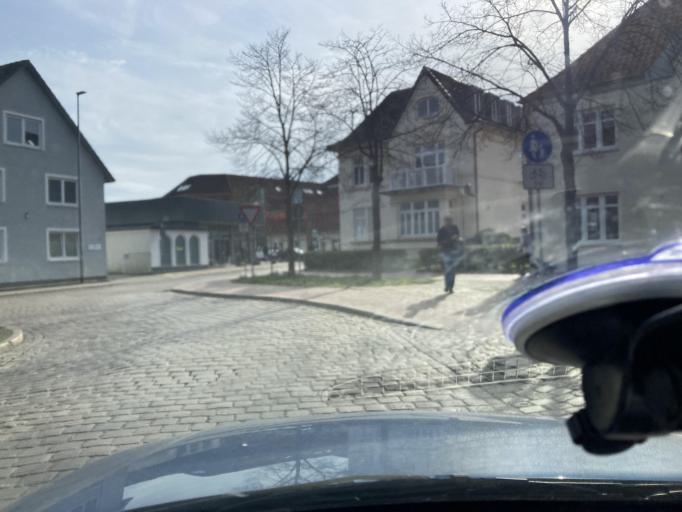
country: DE
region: Schleswig-Holstein
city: Heide
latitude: 54.1926
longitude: 9.0926
